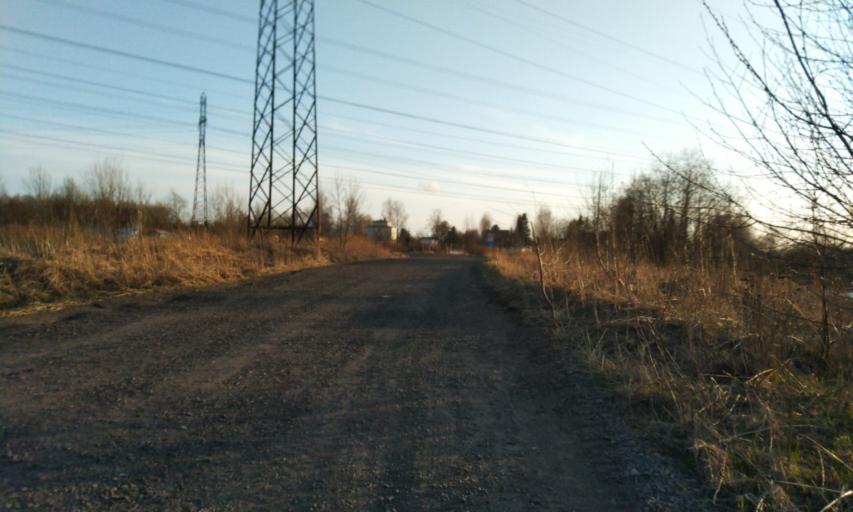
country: RU
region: Leningrad
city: Novoye Devyatkino
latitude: 60.0901
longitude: 30.4591
